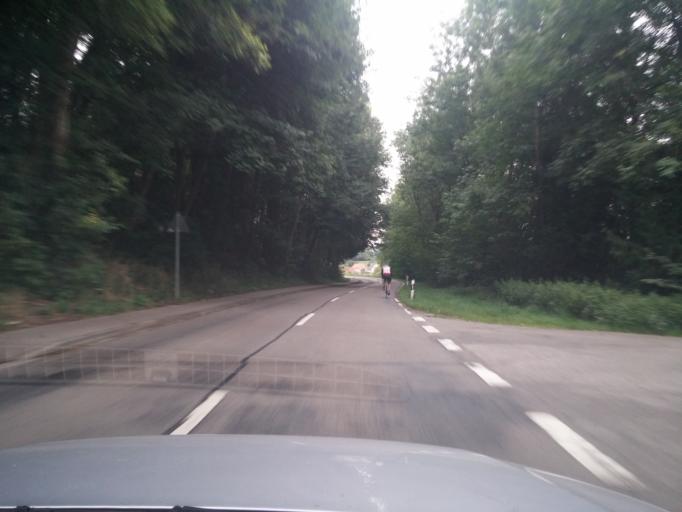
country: DE
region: Bavaria
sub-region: Swabia
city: Buxheim
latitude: 47.9806
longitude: 10.1483
